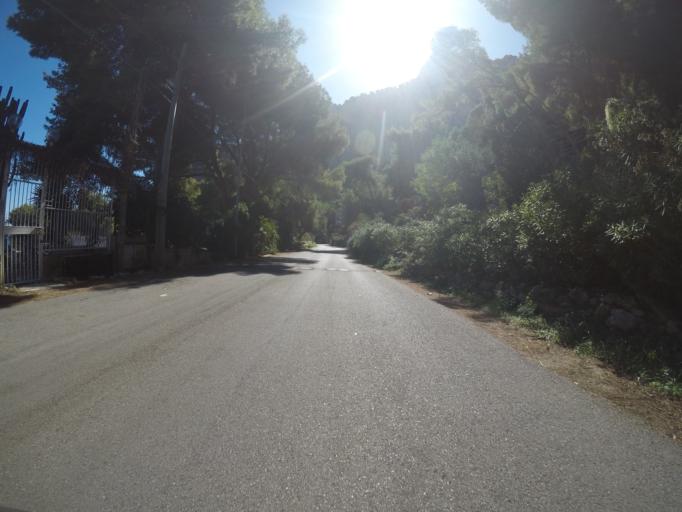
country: IT
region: Sicily
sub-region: Palermo
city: Palermo
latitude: 38.1880
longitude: 13.3432
